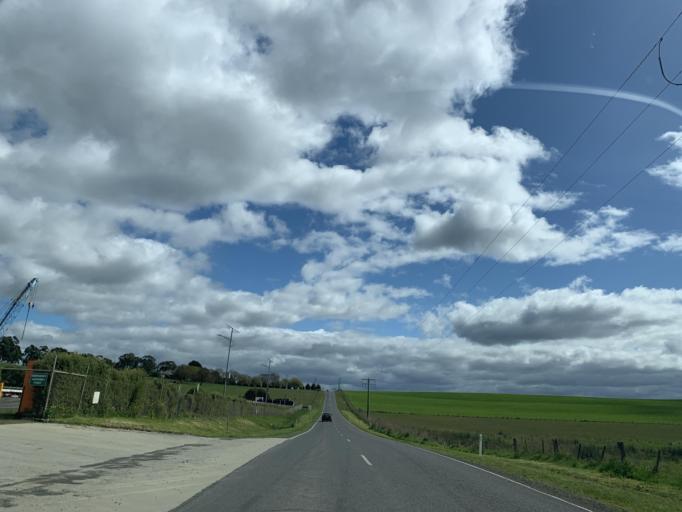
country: AU
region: Victoria
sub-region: Whittlesea
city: Whittlesea
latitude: -37.2807
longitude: 144.9441
